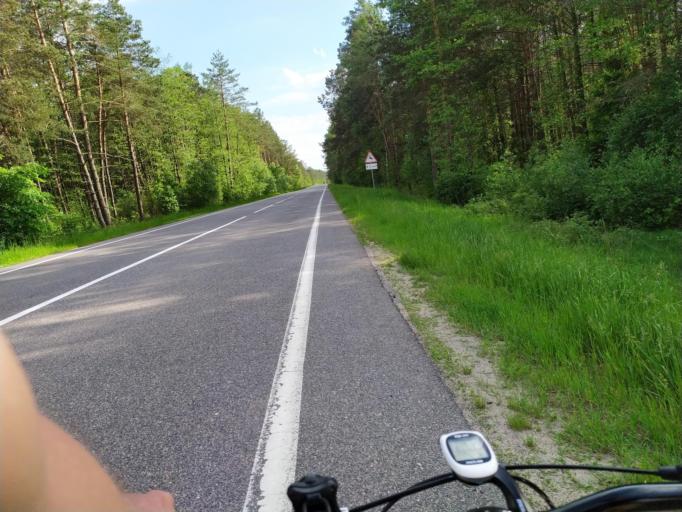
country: BY
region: Brest
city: Zhabinka
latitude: 52.4267
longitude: 24.1236
